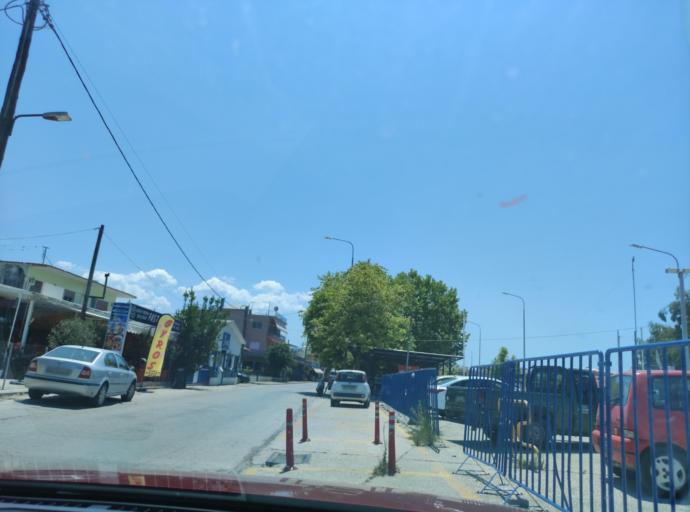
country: GR
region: East Macedonia and Thrace
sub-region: Nomos Kavalas
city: Keramoti
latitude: 40.8572
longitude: 24.7029
